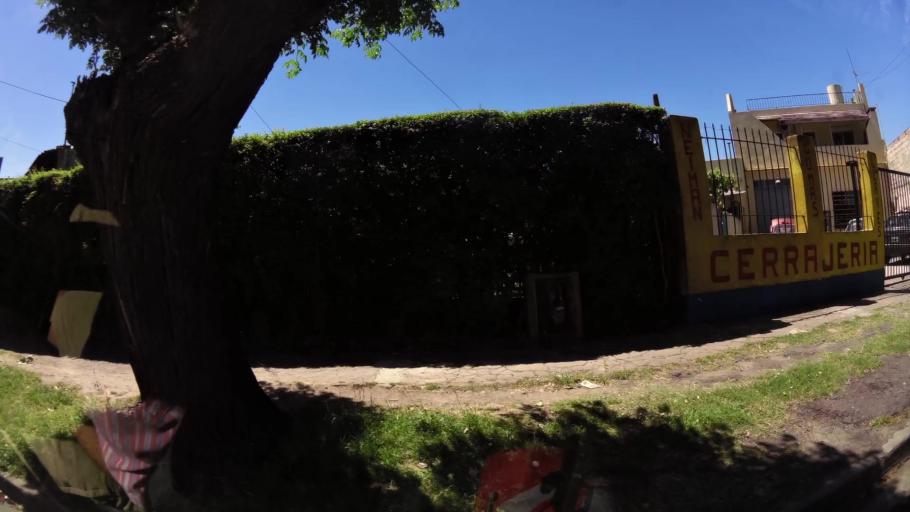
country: AR
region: Buenos Aires
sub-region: Partido de San Isidro
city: San Isidro
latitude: -34.5072
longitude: -58.5701
